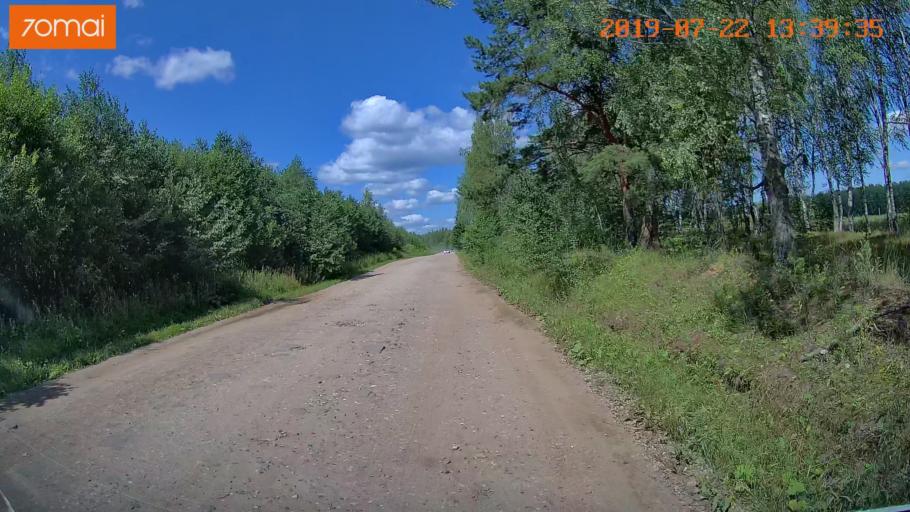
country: RU
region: Ivanovo
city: Novo-Talitsy
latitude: 57.0733
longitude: 40.8816
